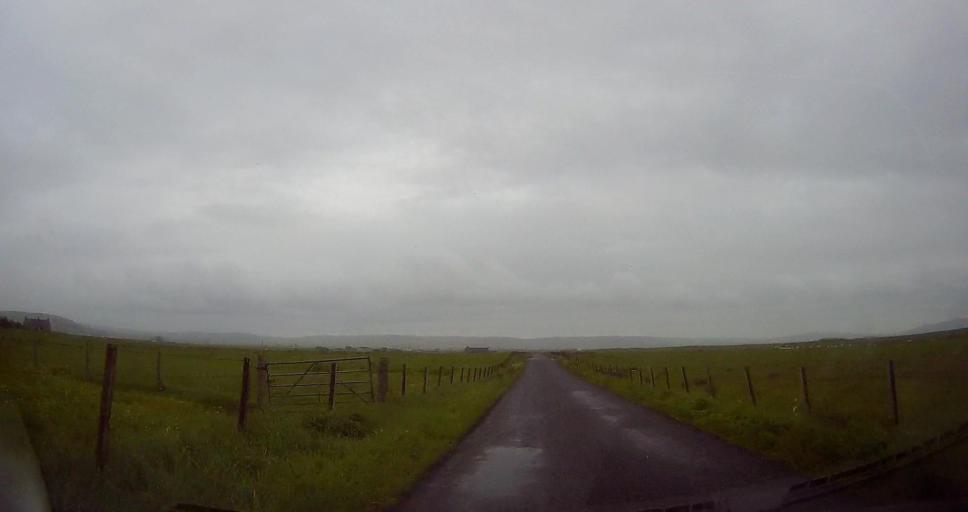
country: GB
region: Scotland
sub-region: Orkney Islands
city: Stromness
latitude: 59.0708
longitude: -3.2912
